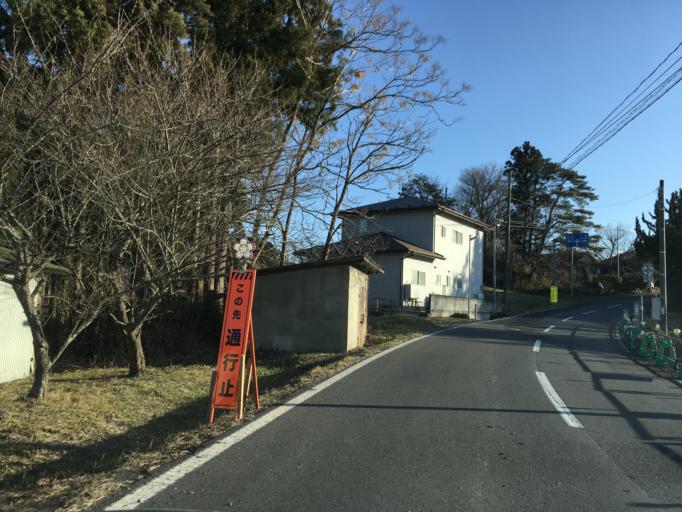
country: JP
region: Iwate
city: Ichinoseki
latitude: 38.7825
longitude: 141.2233
